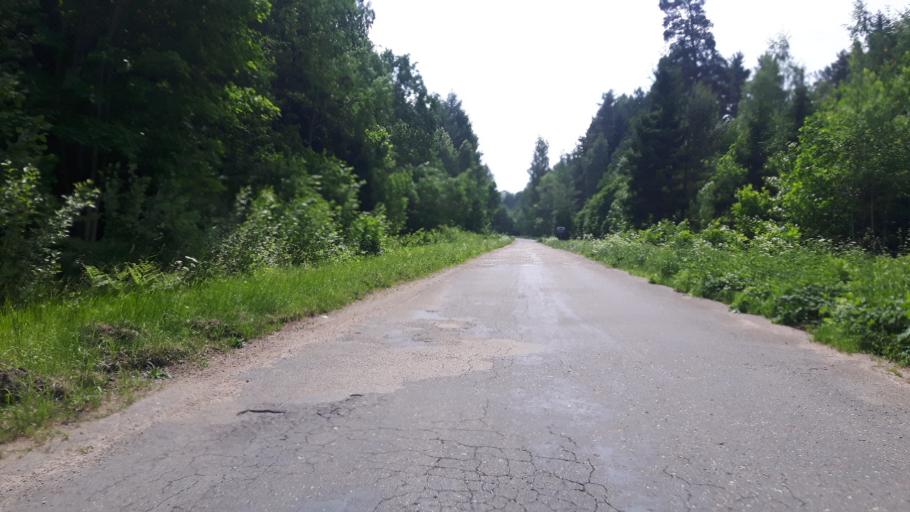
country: LV
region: Saulkrastu
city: Saulkrasti
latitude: 57.4116
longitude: 24.4246
